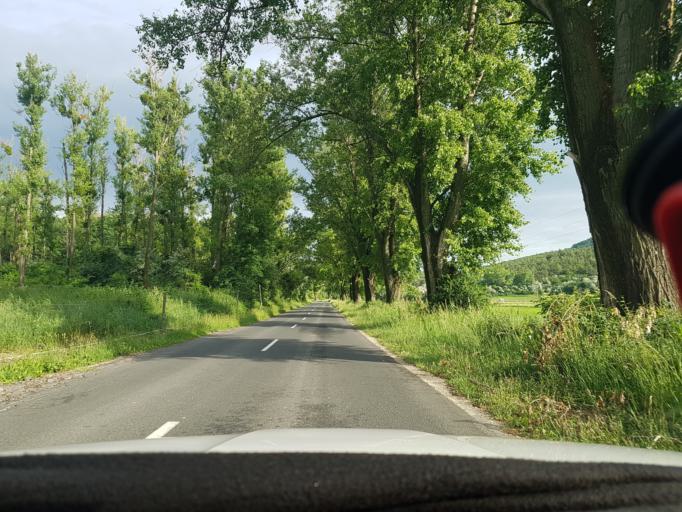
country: HU
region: Komarom-Esztergom
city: Labatlan
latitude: 47.7328
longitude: 18.5281
